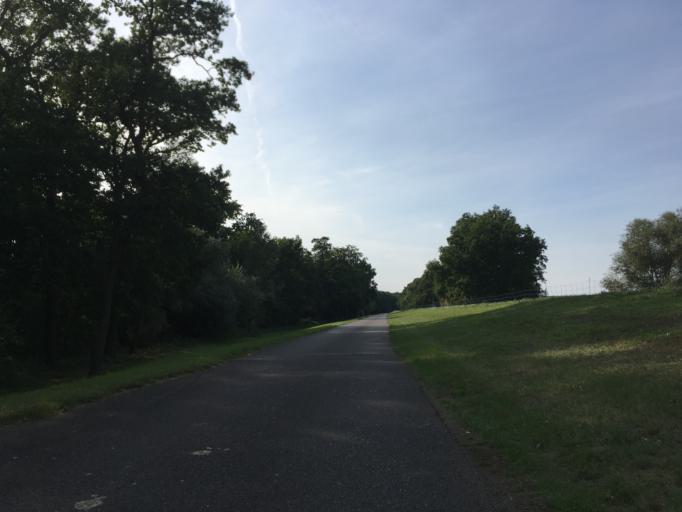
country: DE
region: Brandenburg
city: Brieskow-Finkenheerd
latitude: 52.2699
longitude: 14.6054
